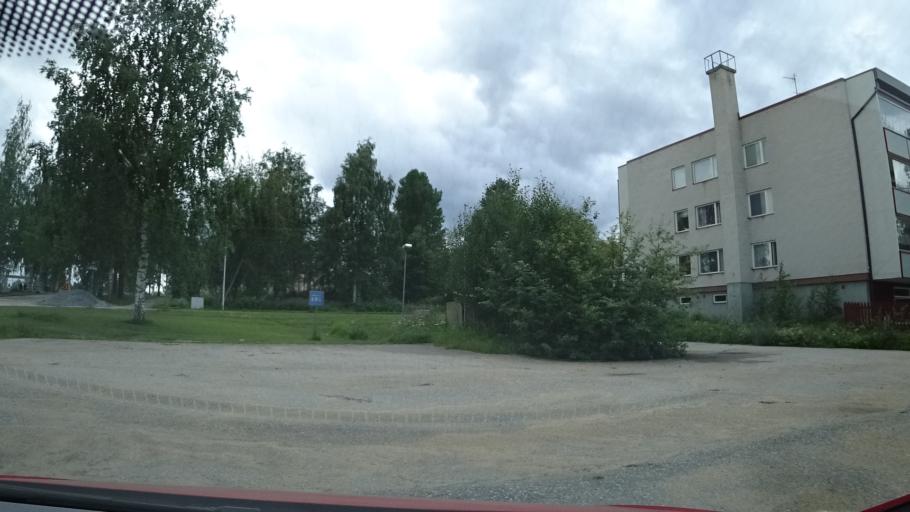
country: FI
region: North Karelia
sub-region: Pielisen Karjala
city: Nurmes
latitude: 63.5435
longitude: 29.1426
